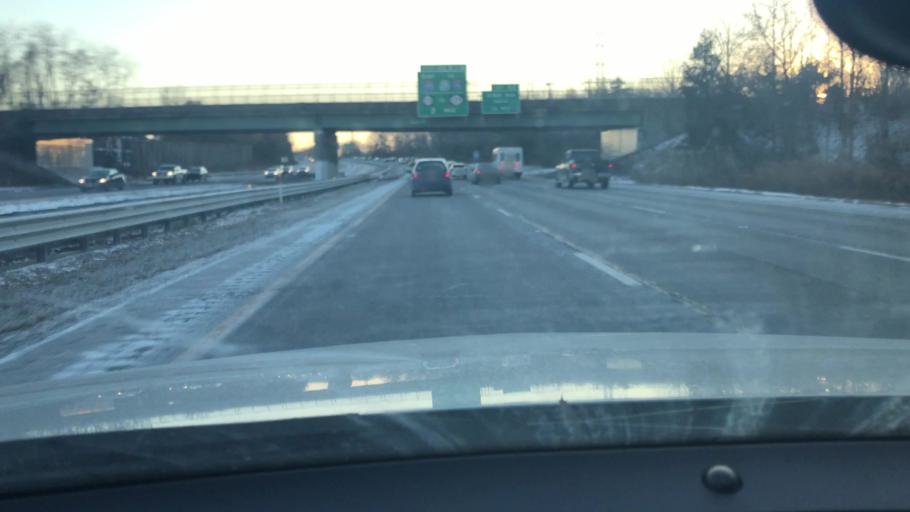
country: US
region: New Jersey
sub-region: Mercer County
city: White Horse
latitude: 40.2124
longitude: -74.7045
